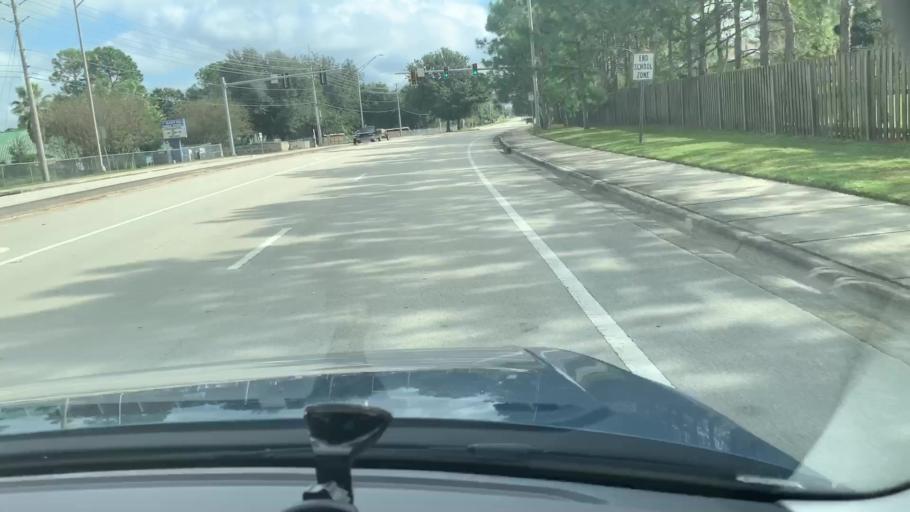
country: US
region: Florida
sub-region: Polk County
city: Gibsonia
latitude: 28.0914
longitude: -81.9934
